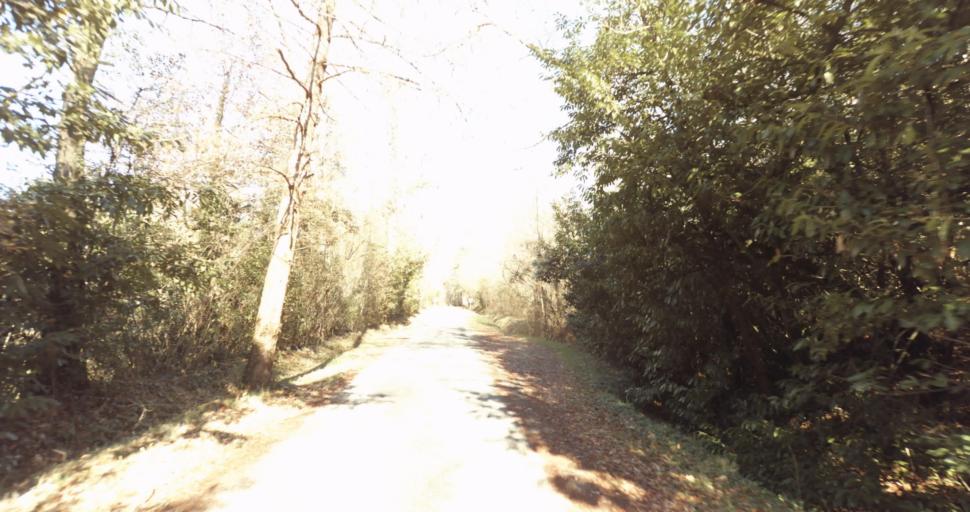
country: FR
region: Aquitaine
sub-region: Departement des Pyrenees-Atlantiques
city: Morlaas
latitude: 43.3330
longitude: -0.2818
